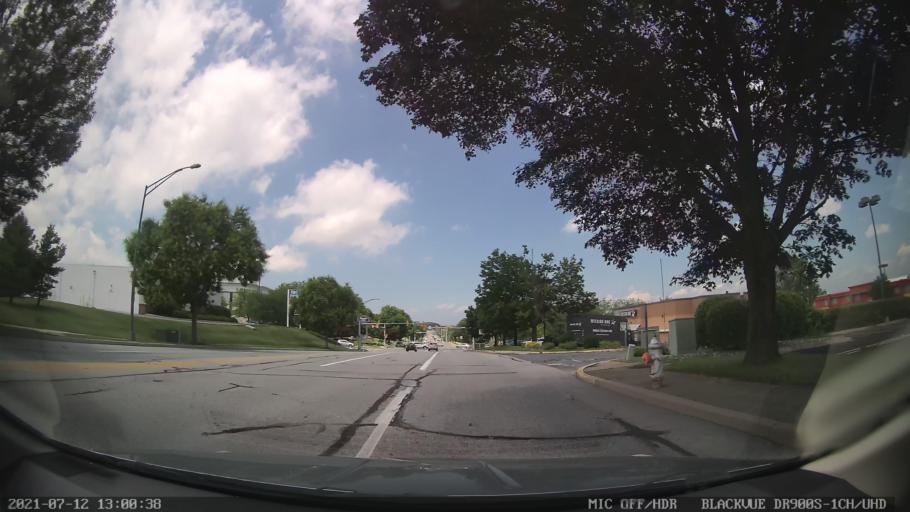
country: US
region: Pennsylvania
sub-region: Berks County
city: Wyomissing Hills
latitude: 40.3466
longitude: -75.9707
